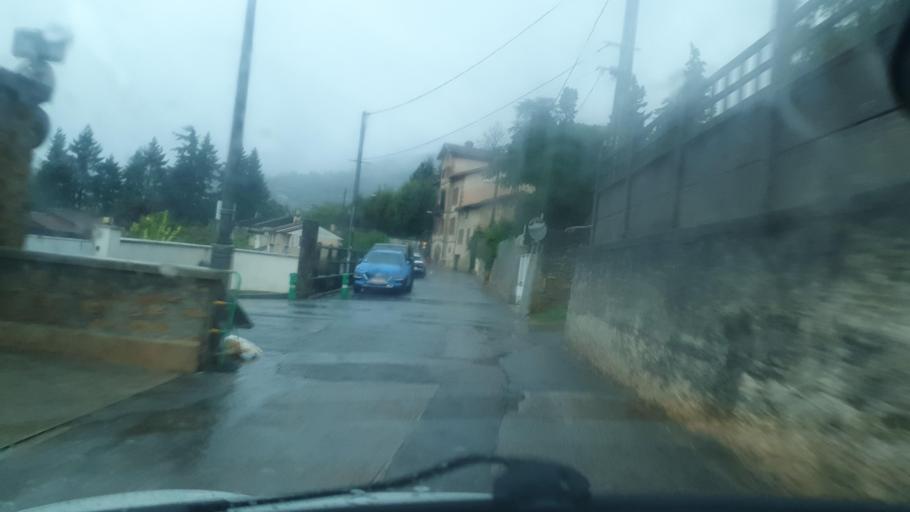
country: FR
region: Rhone-Alpes
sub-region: Departement du Rhone
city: Fontaines-sur-Saone
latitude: 45.8433
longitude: 4.8265
